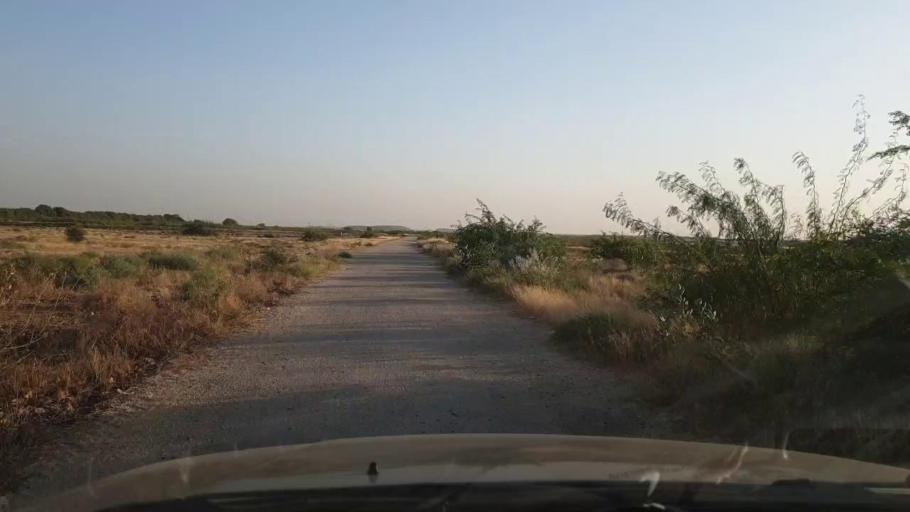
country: PK
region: Sindh
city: Kotri
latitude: 25.2279
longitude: 68.2246
